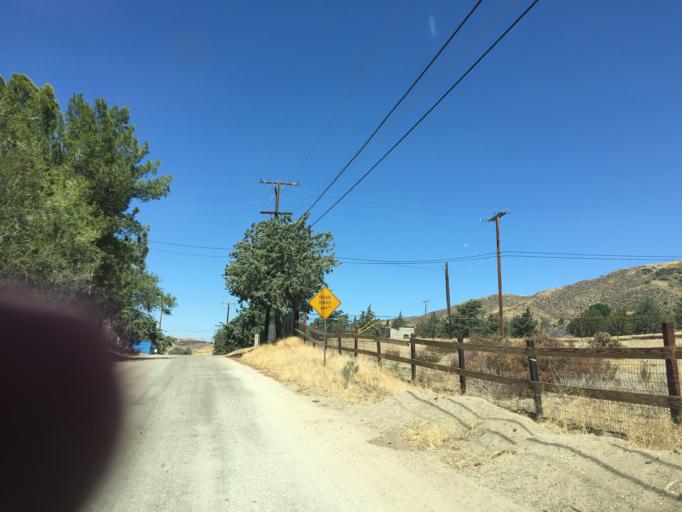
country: US
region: California
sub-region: Los Angeles County
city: Leona Valley
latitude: 34.6283
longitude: -118.3043
